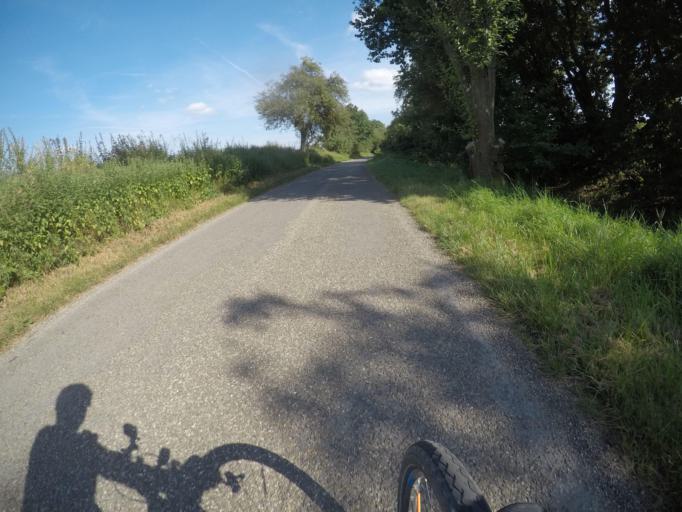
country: DE
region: Baden-Wuerttemberg
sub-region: Karlsruhe Region
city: Olbronn-Durrn
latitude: 48.9517
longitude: 8.7640
